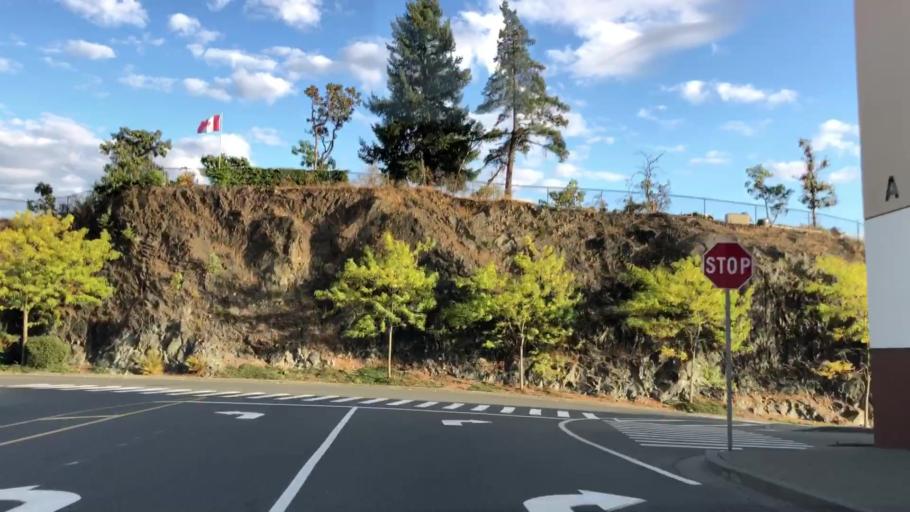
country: CA
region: British Columbia
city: Langford
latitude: 48.4623
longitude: -123.4973
